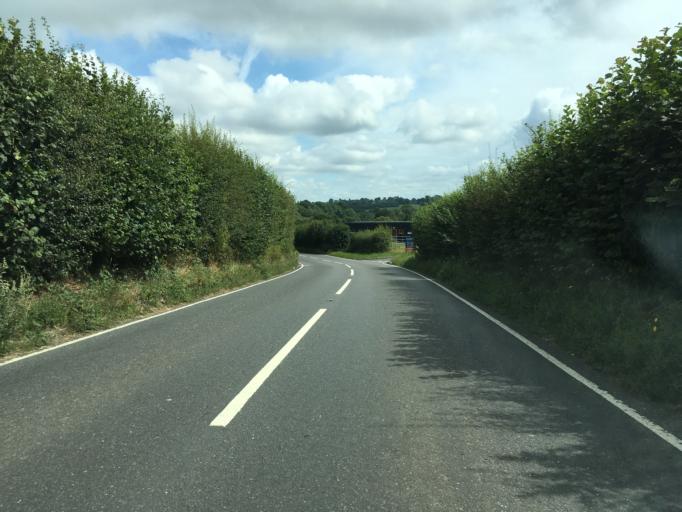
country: GB
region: England
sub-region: Kent
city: Marden
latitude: 51.1106
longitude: 0.4325
